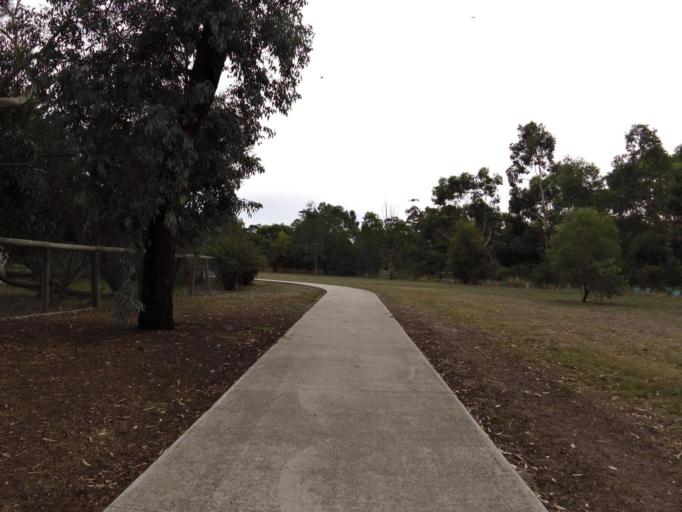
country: AU
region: Victoria
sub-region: Hume
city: Sunbury
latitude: -37.5616
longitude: 144.7239
